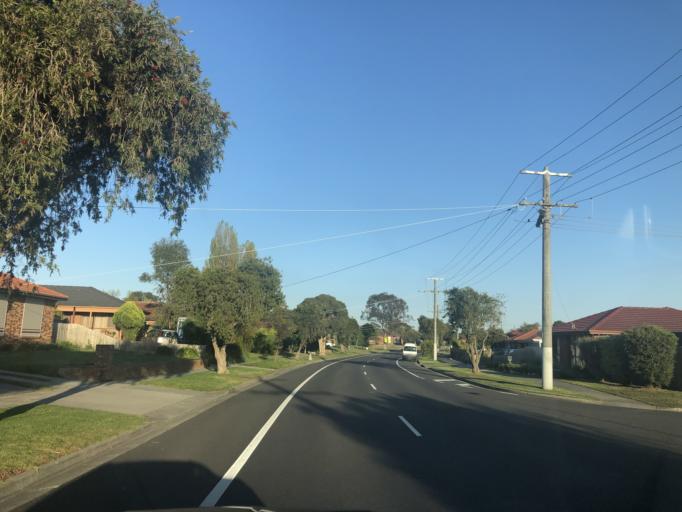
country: AU
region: Victoria
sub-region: Casey
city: Hampton Park
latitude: -38.0402
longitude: 145.2618
